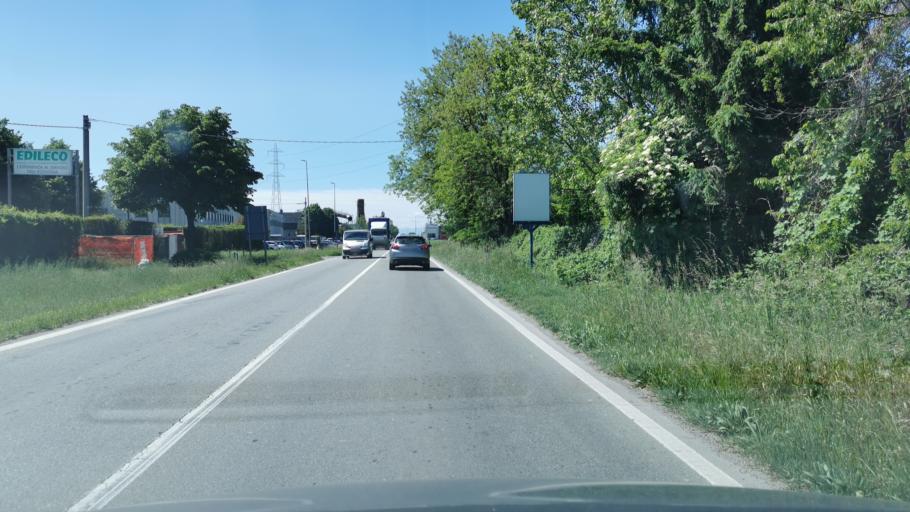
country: IT
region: Piedmont
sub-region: Provincia di Torino
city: Settimo Torinese
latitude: 45.1514
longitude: 7.7480
